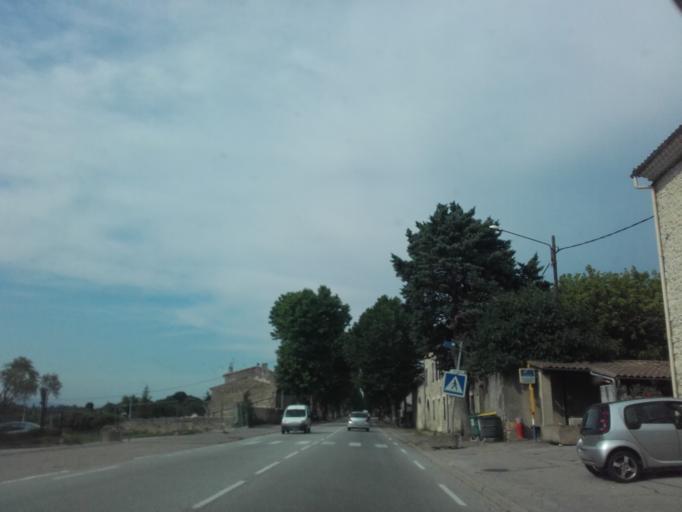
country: FR
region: Rhone-Alpes
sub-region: Departement de l'Ardeche
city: Cruas
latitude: 44.6395
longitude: 4.7753
